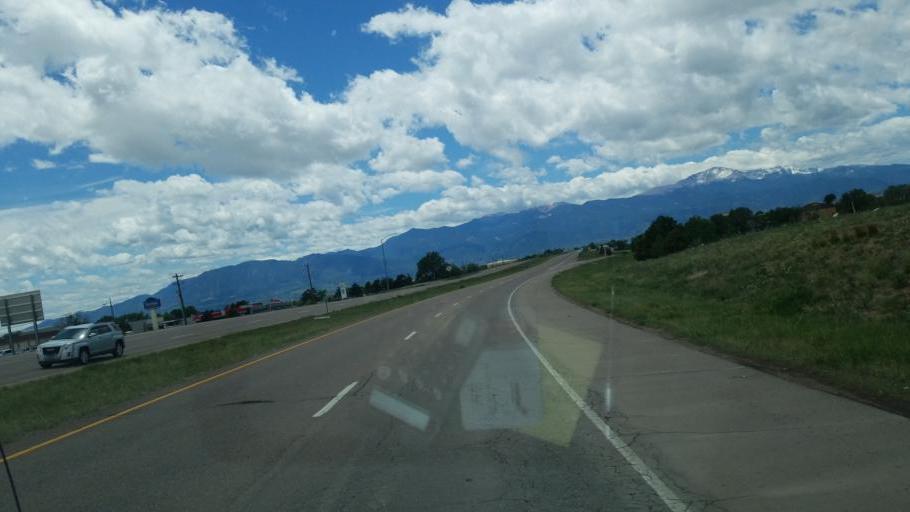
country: US
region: Colorado
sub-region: El Paso County
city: Cimarron Hills
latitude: 38.8403
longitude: -104.6966
